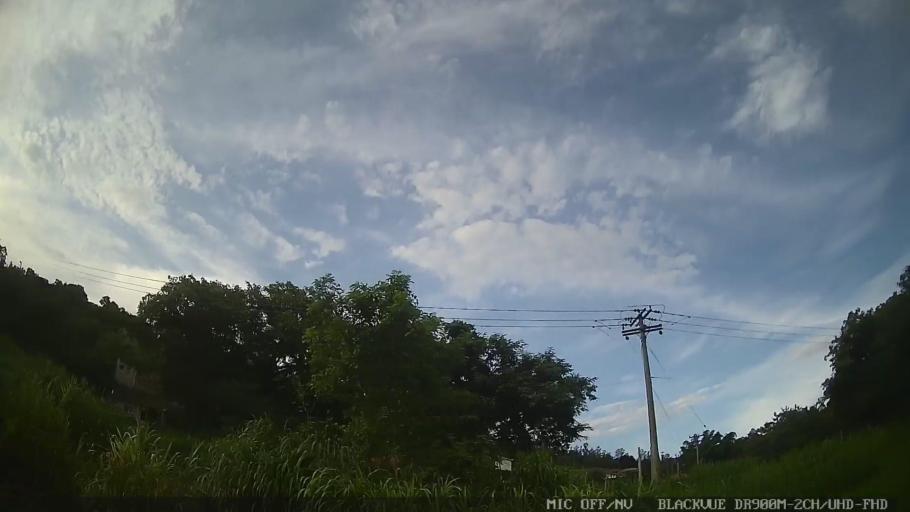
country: BR
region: Sao Paulo
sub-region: Amparo
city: Amparo
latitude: -22.6919
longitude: -46.7256
